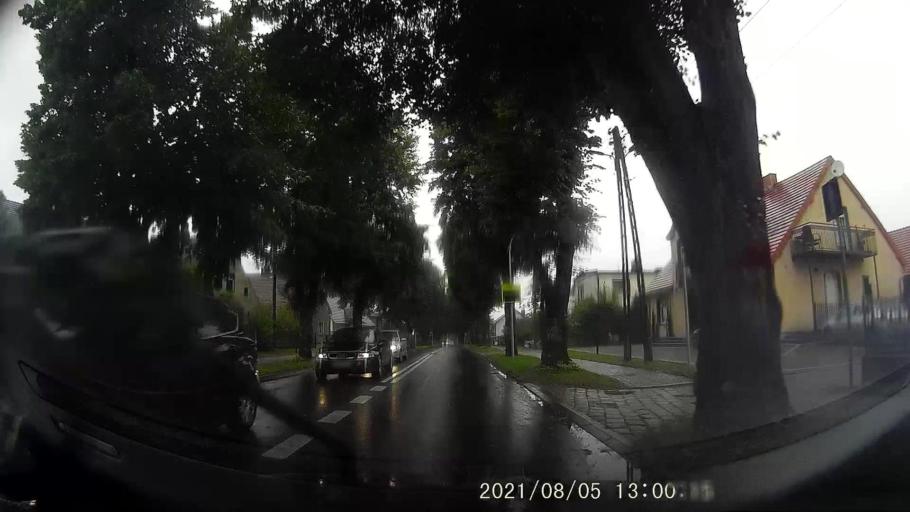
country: PL
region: Opole Voivodeship
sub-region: Powiat krapkowicki
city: Krapkowice
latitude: 50.4802
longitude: 17.9834
